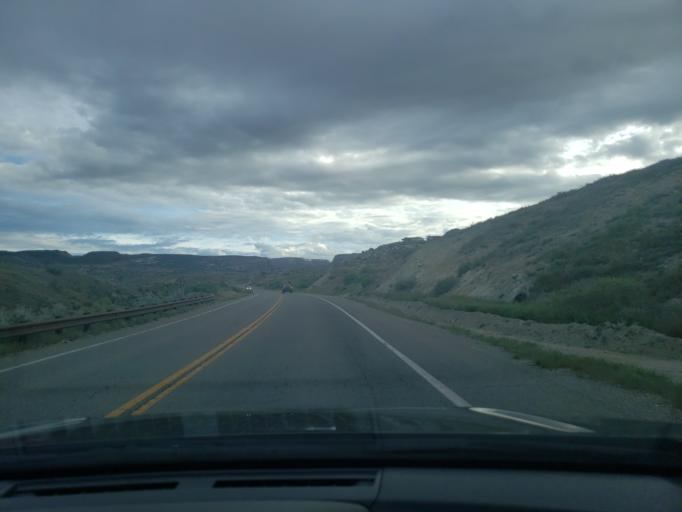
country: US
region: Colorado
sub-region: Mesa County
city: Redlands
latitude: 39.0538
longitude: -108.6021
